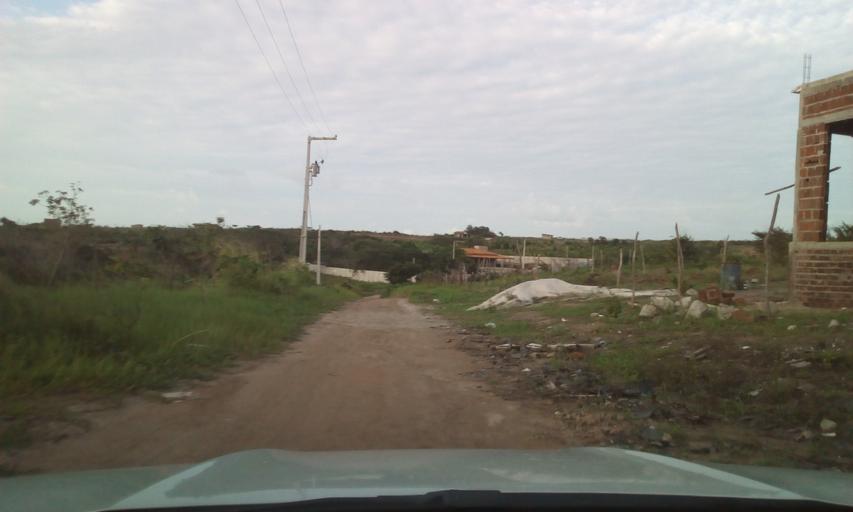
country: BR
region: Paraiba
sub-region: Conde
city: Conde
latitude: -7.2218
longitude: -34.8101
